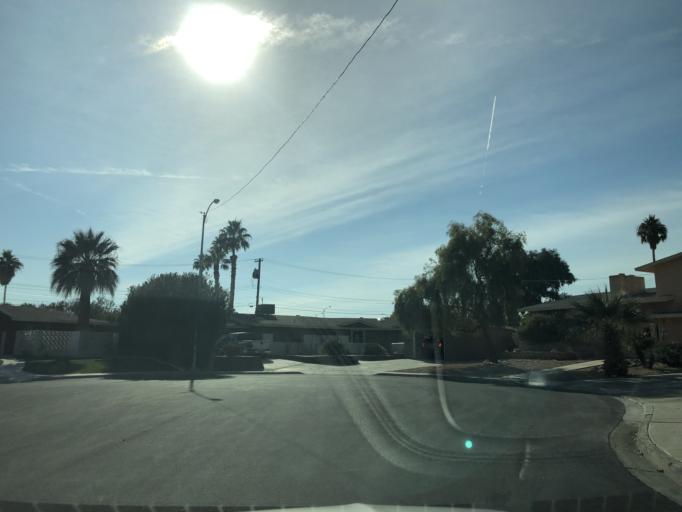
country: US
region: Nevada
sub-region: Clark County
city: Winchester
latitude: 36.1232
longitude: -115.1322
